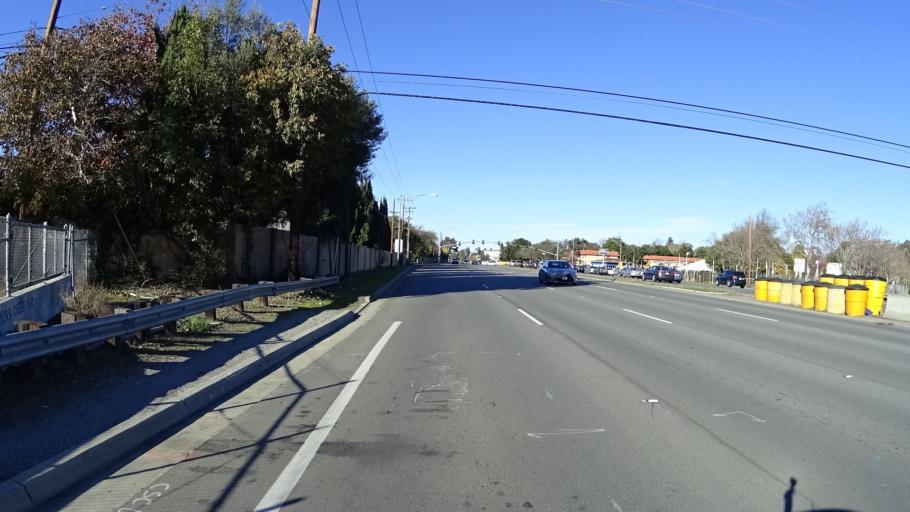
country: US
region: California
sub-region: Santa Clara County
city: Cupertino
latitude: 37.3439
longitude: -121.9959
